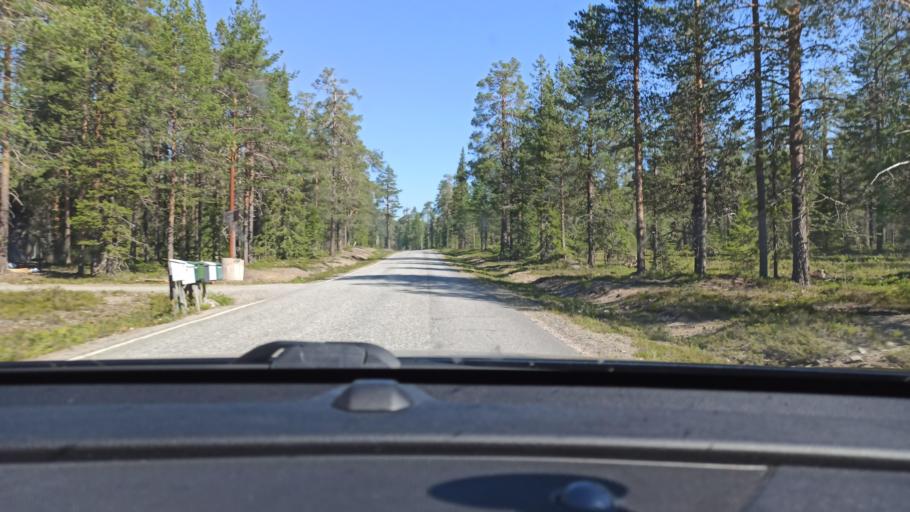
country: FI
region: Lapland
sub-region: Tunturi-Lappi
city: Kolari
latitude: 67.6578
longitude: 24.1651
